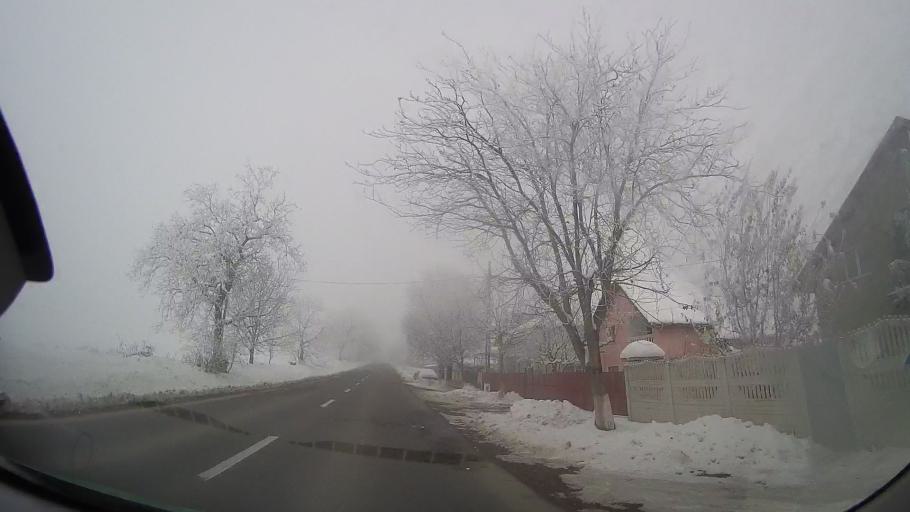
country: RO
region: Iasi
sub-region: Comuna Valea Seaca
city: Valea Seaca
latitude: 47.2907
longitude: 26.6765
